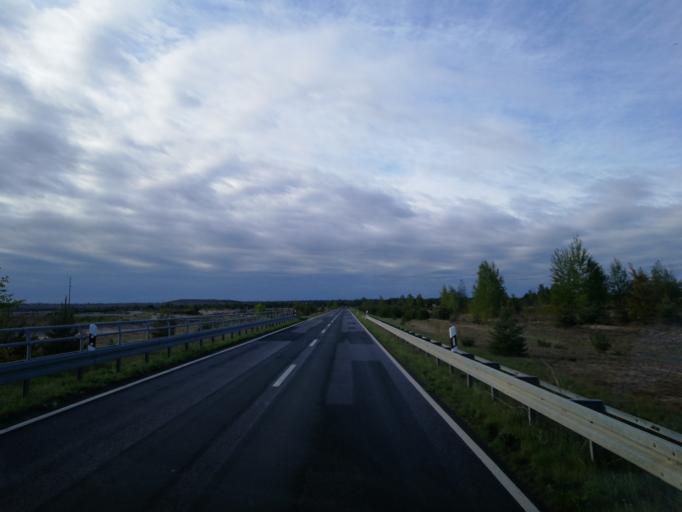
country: DE
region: Brandenburg
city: Sallgast
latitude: 51.5705
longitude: 13.7778
